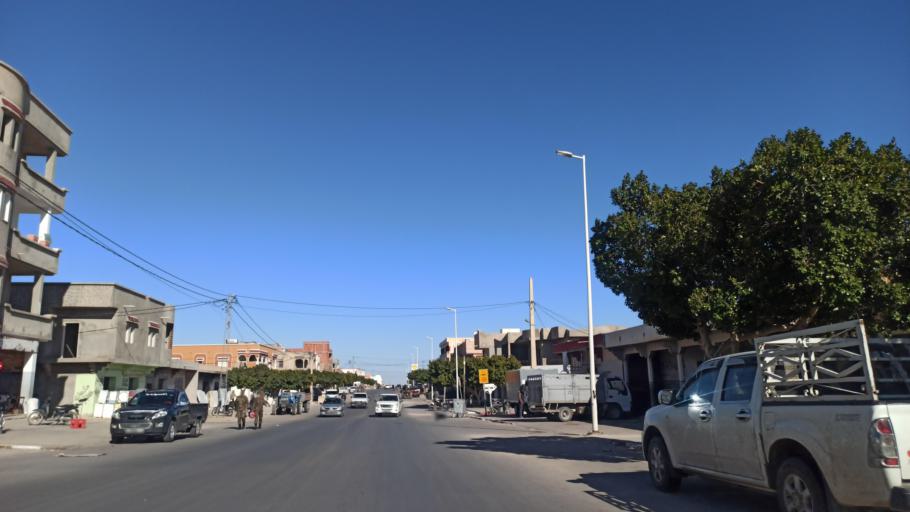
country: TN
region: Sidi Bu Zayd
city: Bi'r al Hufayy
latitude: 34.9373
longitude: 9.2002
